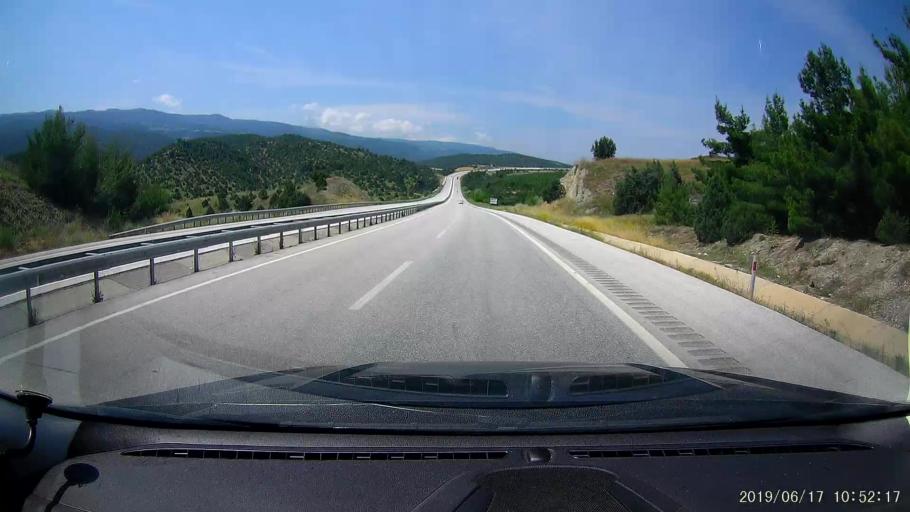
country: TR
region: Corum
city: Hacihamza
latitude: 41.0918
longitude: 34.3445
